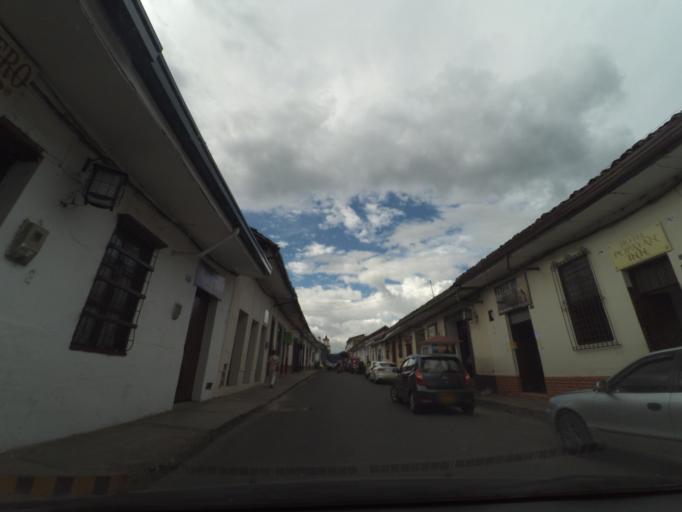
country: CO
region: Cauca
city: Popayan
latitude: 2.4393
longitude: -76.6083
